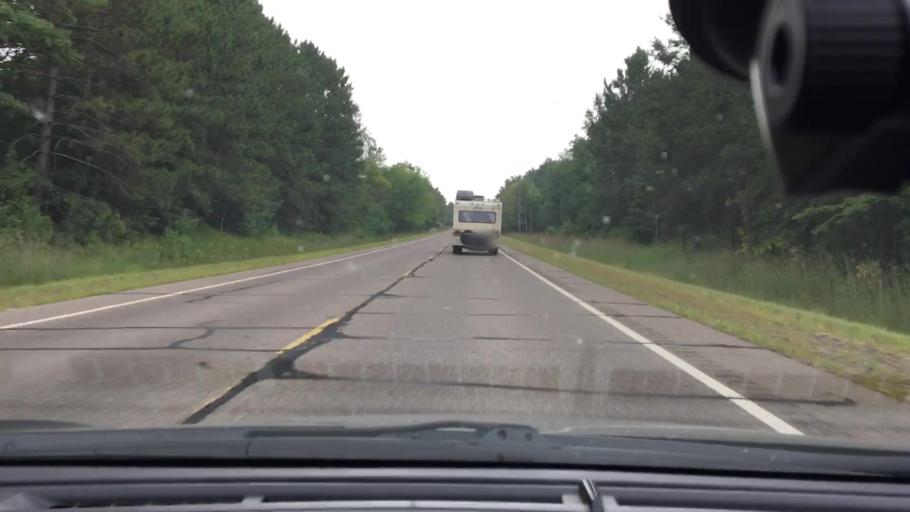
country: US
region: Minnesota
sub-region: Crow Wing County
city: Crosby
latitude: 46.4405
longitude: -93.8766
